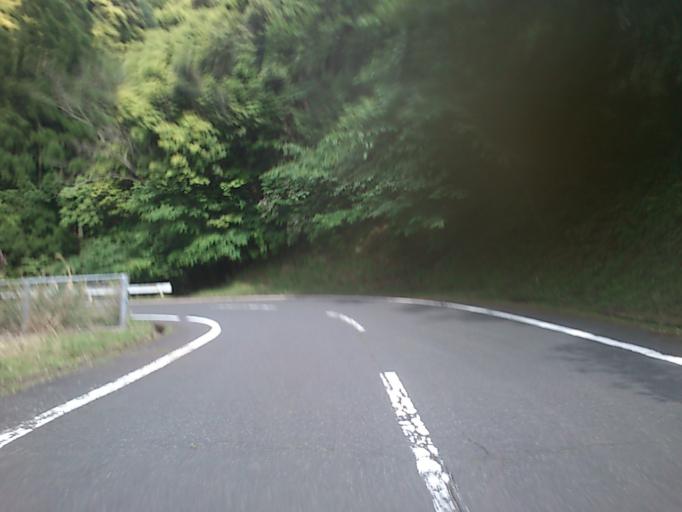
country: JP
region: Hyogo
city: Toyooka
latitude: 35.6870
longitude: 134.9878
